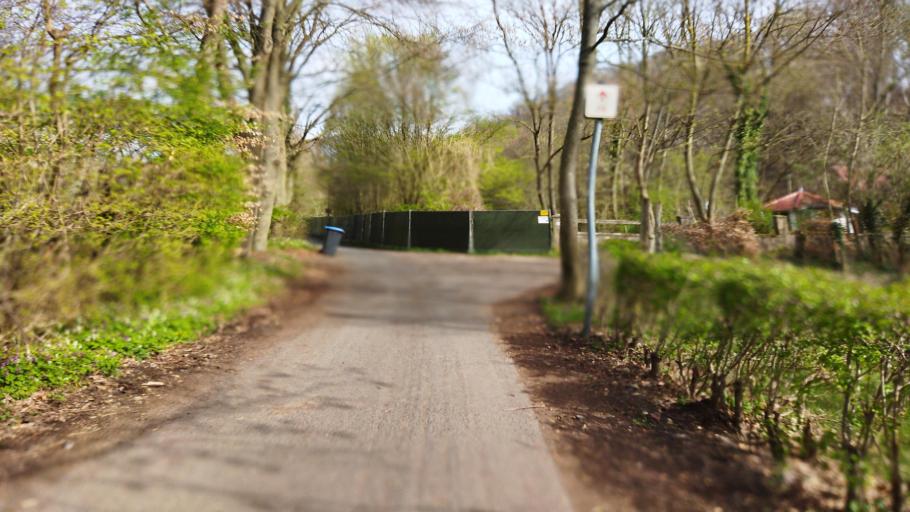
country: DE
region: North Rhine-Westphalia
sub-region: Regierungsbezirk Detmold
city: Vlotho
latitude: 52.1936
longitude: 8.8651
